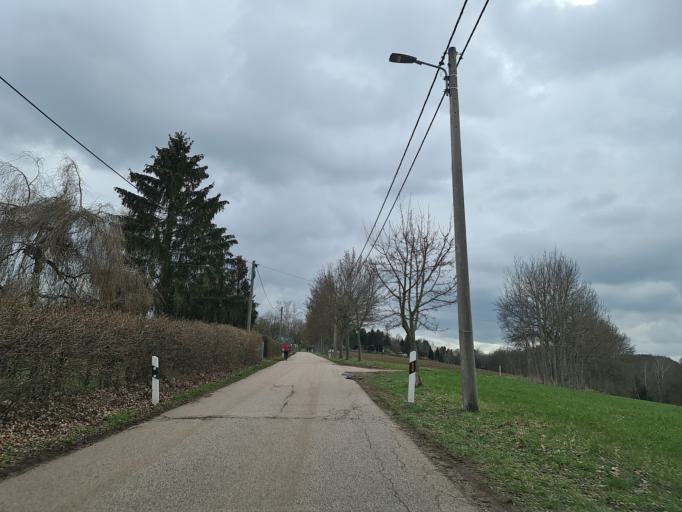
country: DE
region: Saxony
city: Lichtenstein
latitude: 50.7425
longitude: 12.6238
